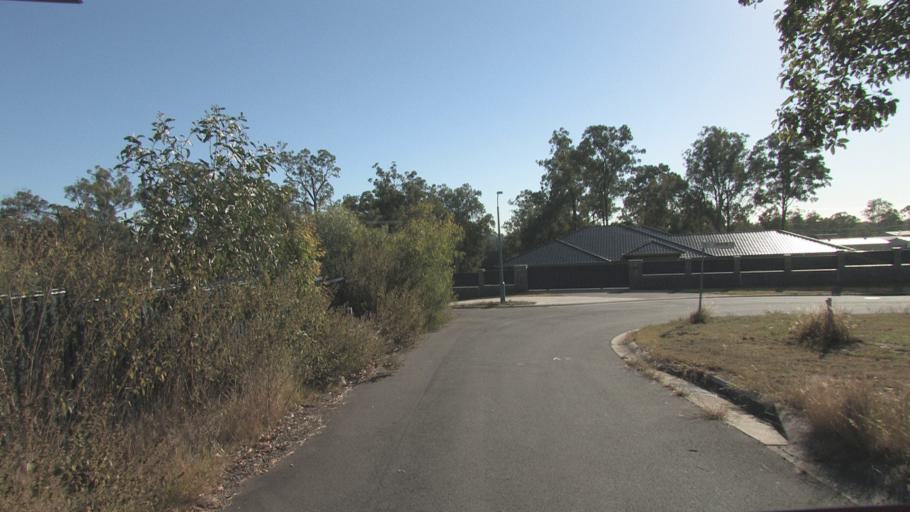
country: AU
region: Queensland
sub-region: Brisbane
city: Forest Lake
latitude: -27.6528
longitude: 152.9856
